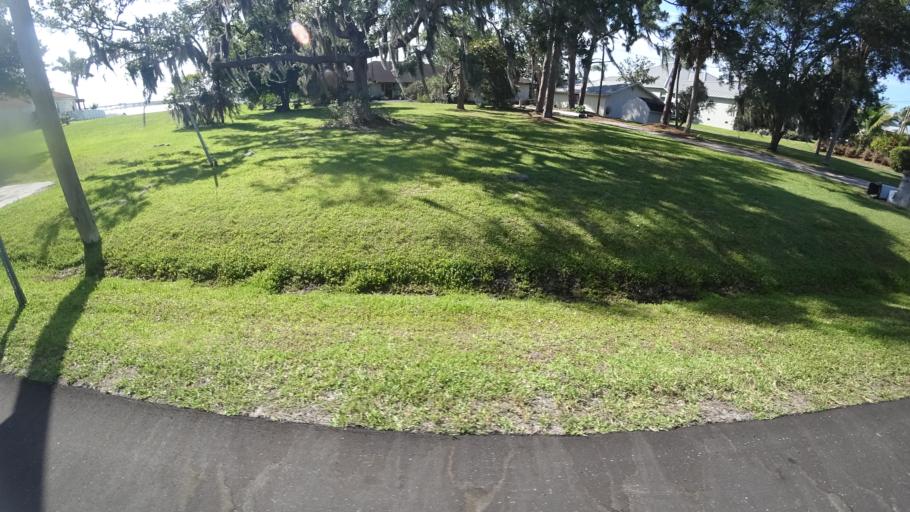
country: US
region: Florida
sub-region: Manatee County
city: Ellenton
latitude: 27.5206
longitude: -82.5150
